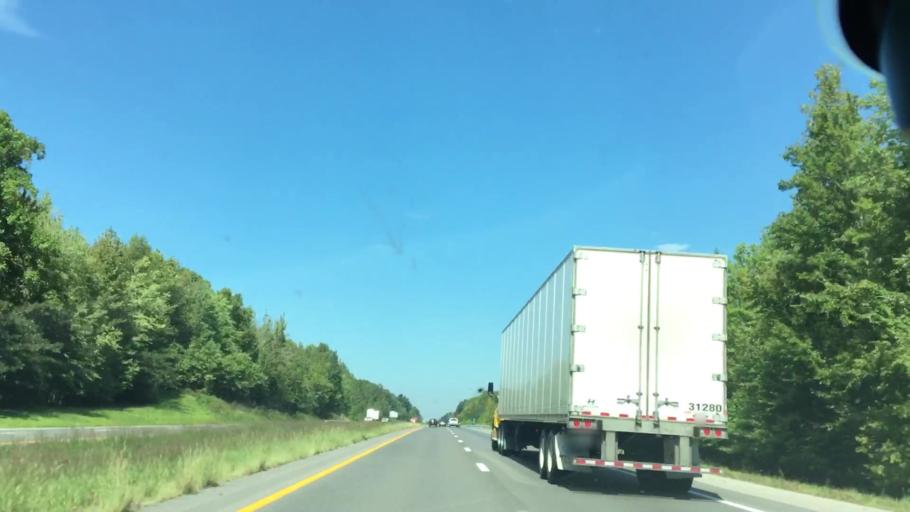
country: US
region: Kentucky
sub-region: Hopkins County
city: Earlington
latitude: 37.2663
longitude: -87.4533
